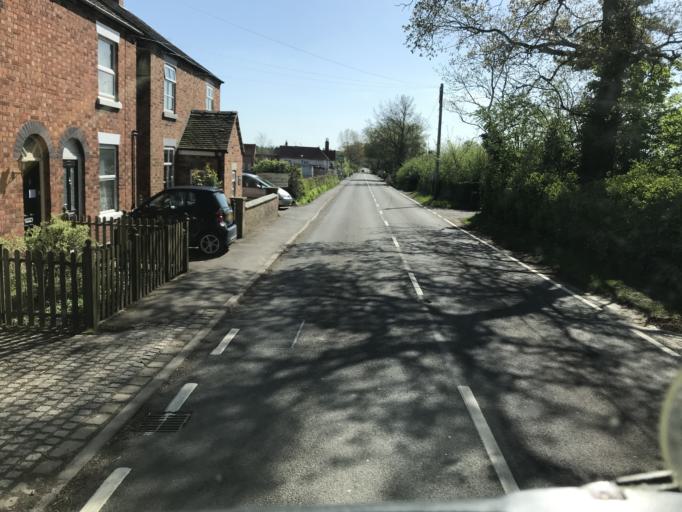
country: GB
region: England
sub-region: Cheshire East
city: Nantwich
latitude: 53.1065
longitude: -2.5120
